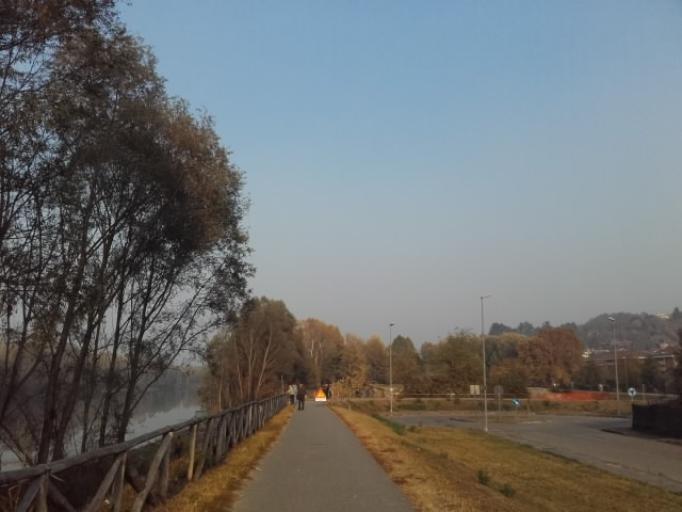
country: IT
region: Piedmont
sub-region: Provincia di Torino
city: San Mauro Torinese
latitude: 45.0932
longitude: 7.7470
